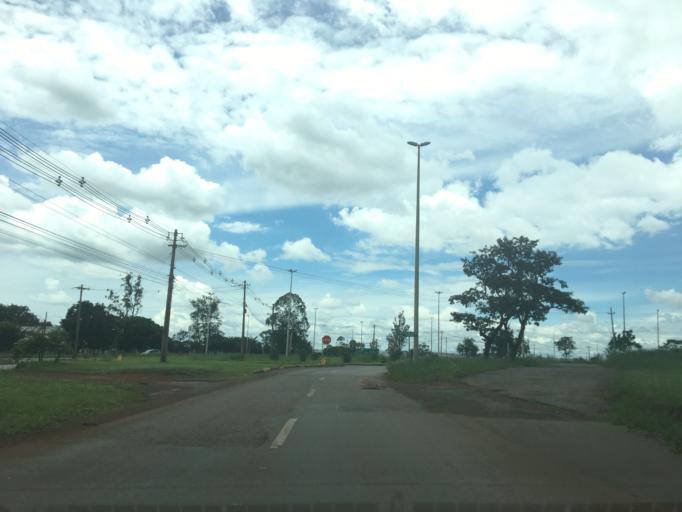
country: BR
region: Federal District
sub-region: Brasilia
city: Brasilia
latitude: -15.8320
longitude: -47.9408
